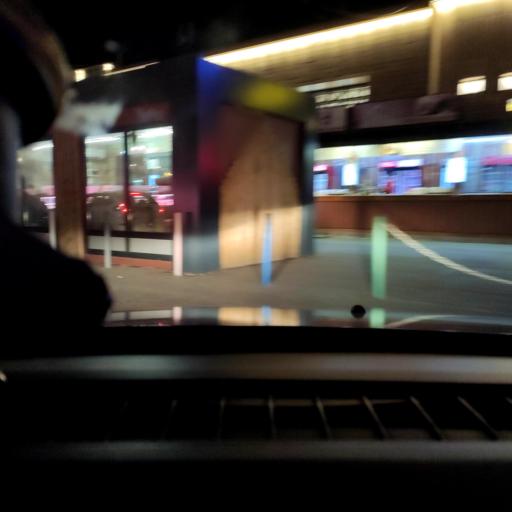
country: RU
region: Samara
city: Samara
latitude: 53.1413
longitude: 50.1762
